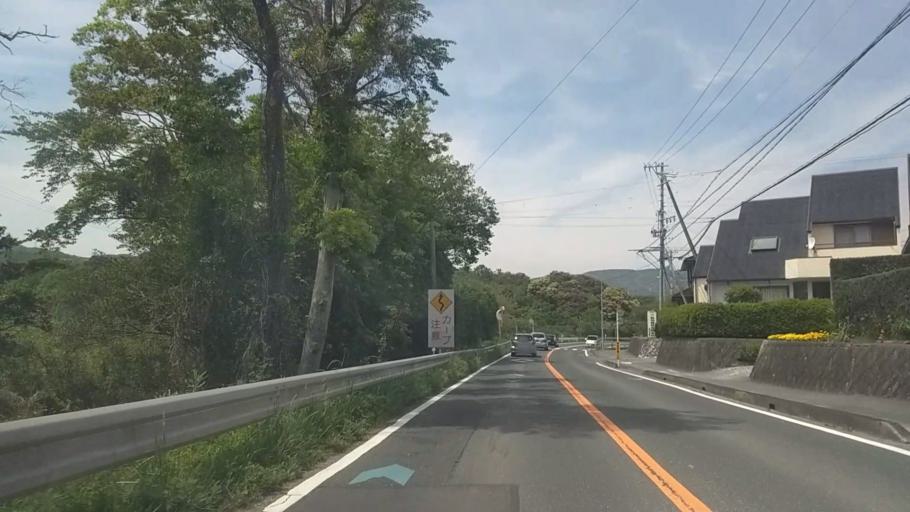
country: JP
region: Shizuoka
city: Kosai-shi
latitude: 34.7479
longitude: 137.5126
